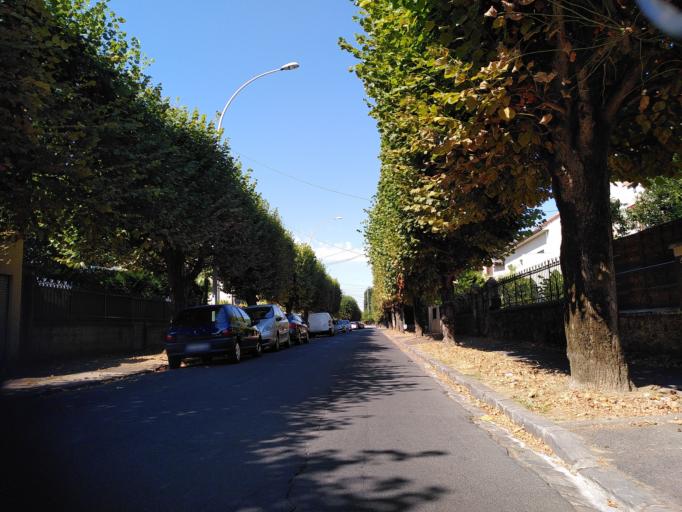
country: FR
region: Ile-de-France
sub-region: Departement de l'Essonne
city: Savigny-sur-Orge
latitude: 48.6912
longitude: 2.3538
